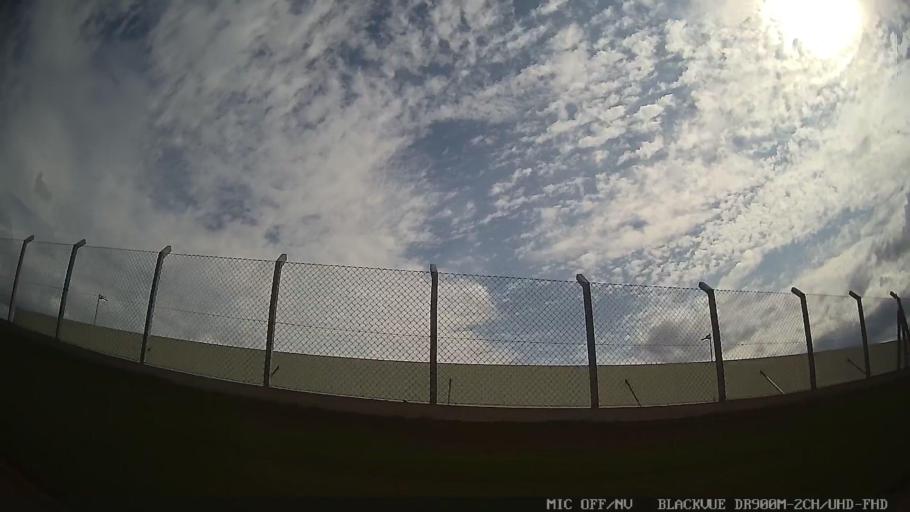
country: BR
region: Sao Paulo
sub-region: Salto
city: Salto
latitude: -23.1607
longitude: -47.2653
